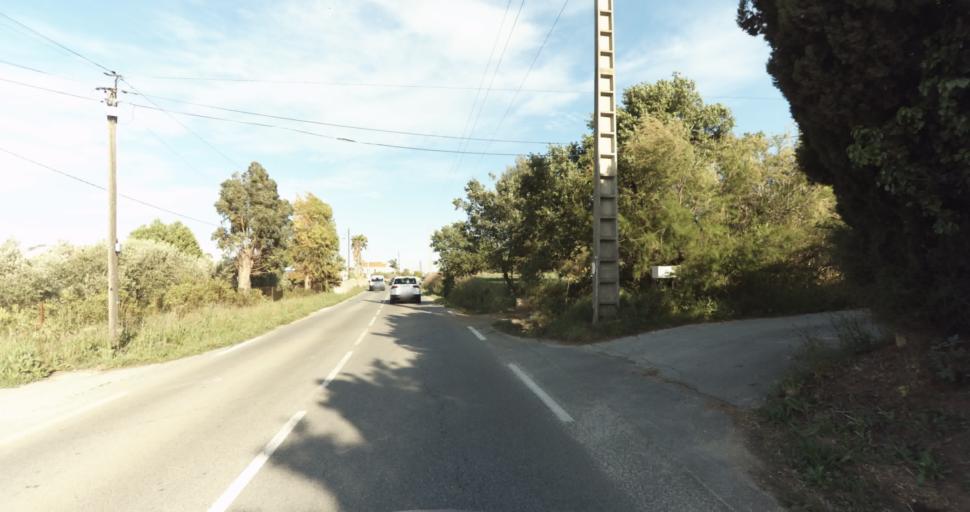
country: FR
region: Provence-Alpes-Cote d'Azur
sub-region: Departement du Var
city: Carqueiranne
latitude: 43.1161
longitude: 6.0915
